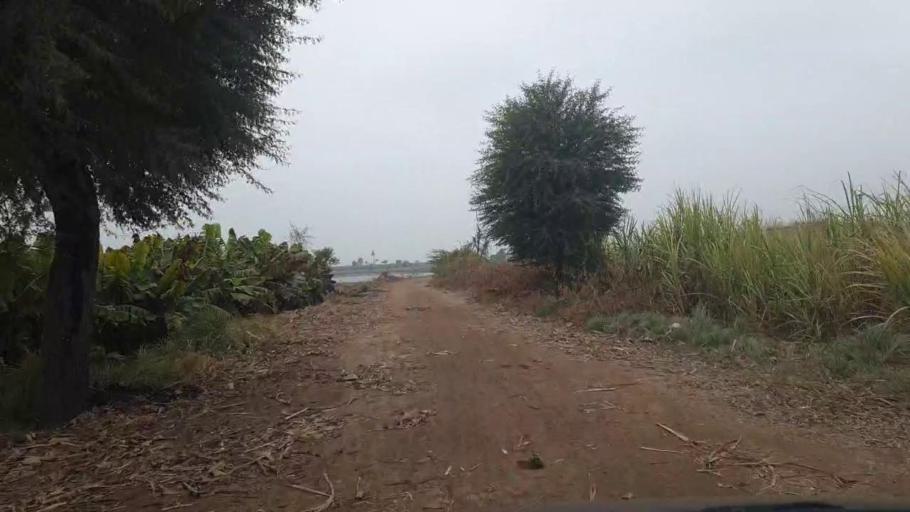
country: PK
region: Sindh
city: Tando Adam
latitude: 25.8316
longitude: 68.7223
